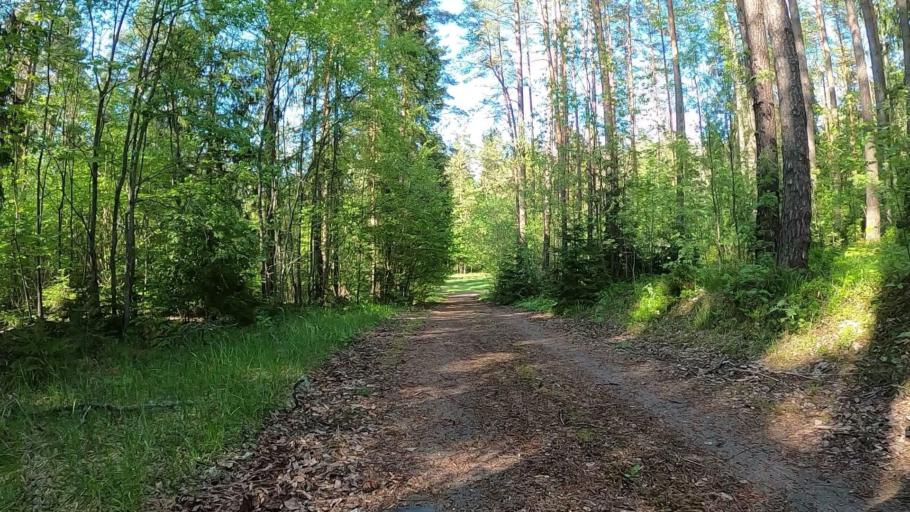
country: LV
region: Baldone
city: Baldone
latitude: 56.7754
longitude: 24.4101
